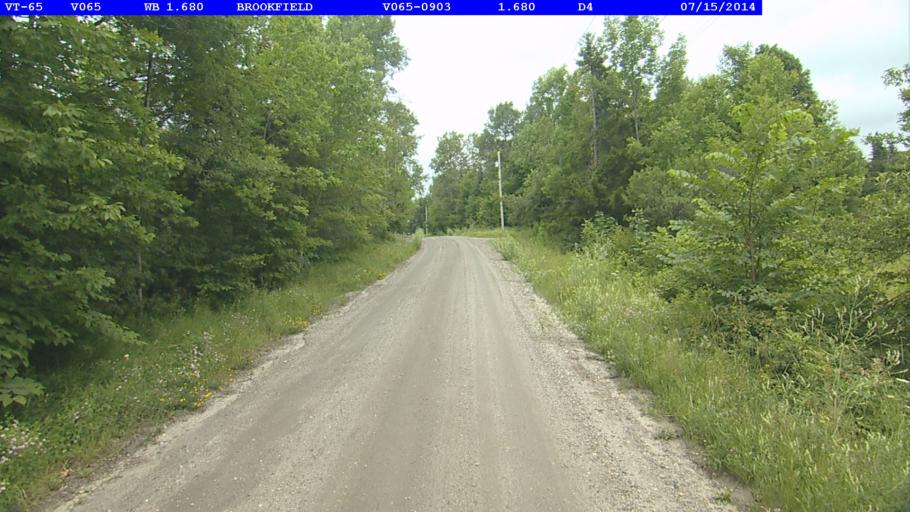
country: US
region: Vermont
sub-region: Washington County
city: Northfield
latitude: 44.0466
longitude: -72.6256
